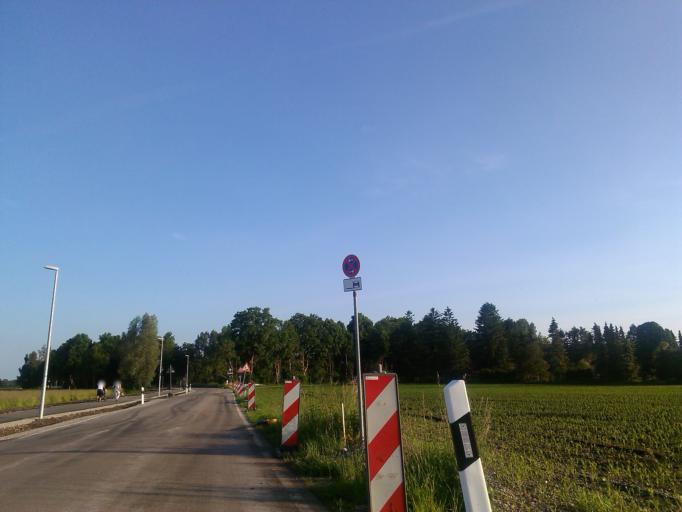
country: DE
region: Bavaria
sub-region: Upper Bavaria
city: Grobenzell
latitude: 48.1905
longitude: 11.4083
